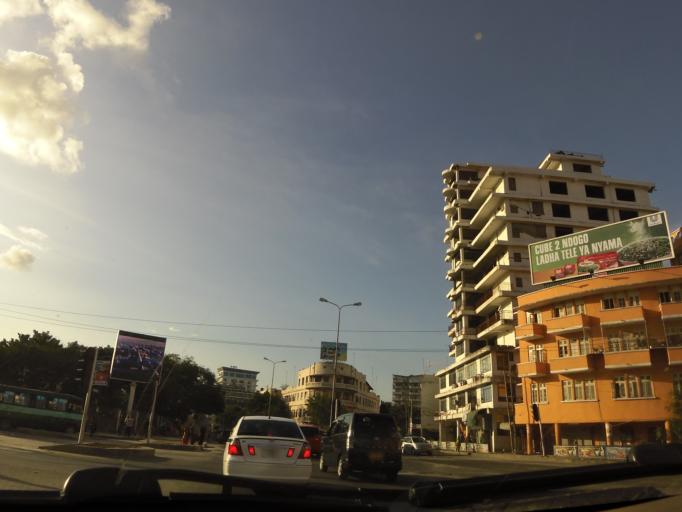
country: TZ
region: Dar es Salaam
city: Dar es Salaam
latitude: -6.8216
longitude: 39.2812
